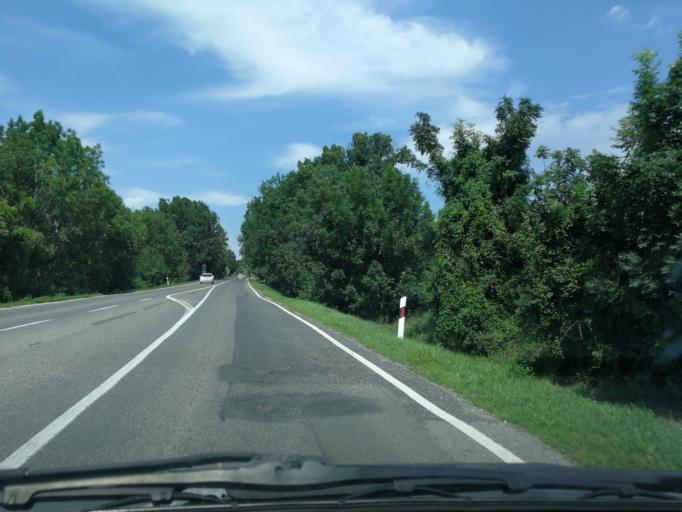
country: HU
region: Baranya
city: Hosszuheteny
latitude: 46.1267
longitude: 18.3693
